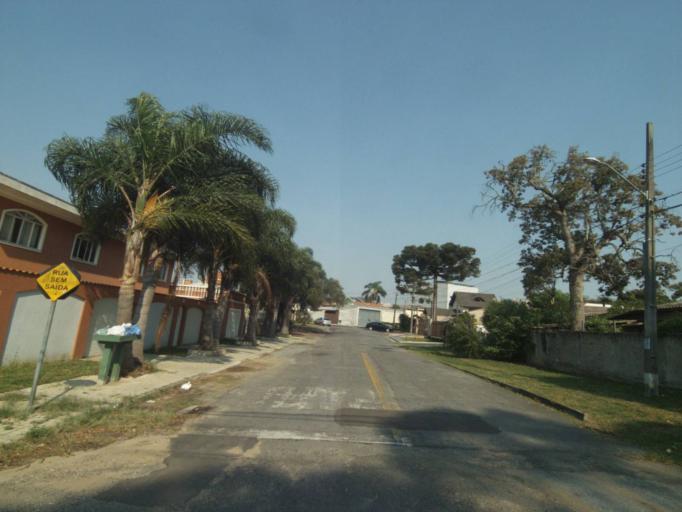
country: BR
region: Parana
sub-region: Sao Jose Dos Pinhais
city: Sao Jose dos Pinhais
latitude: -25.5018
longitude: -49.2752
